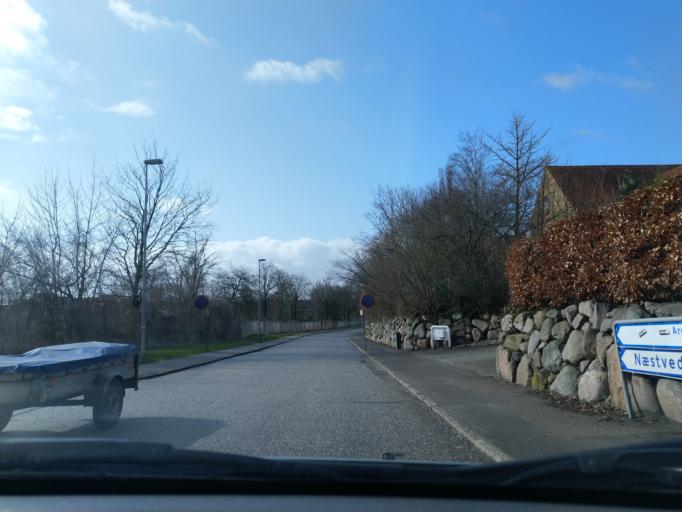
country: DK
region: Zealand
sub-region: Naestved Kommune
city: Naestved
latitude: 55.2235
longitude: 11.7691
